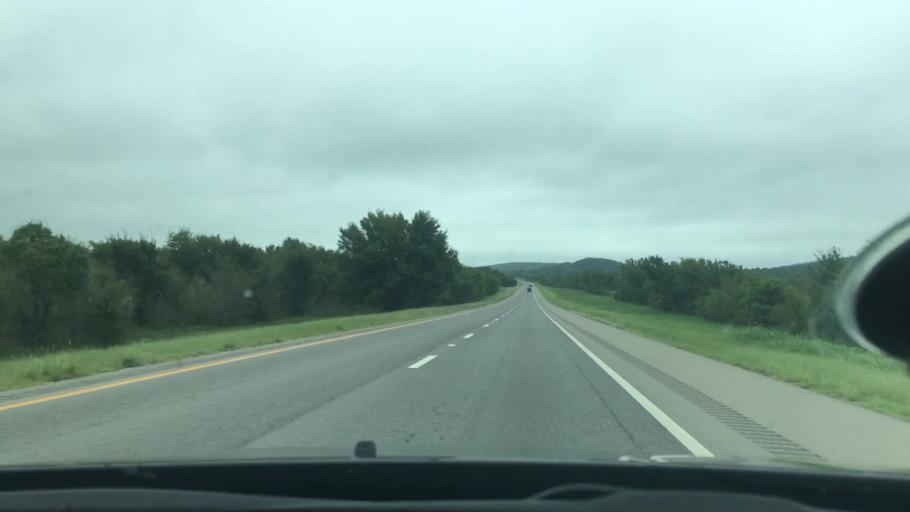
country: US
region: Oklahoma
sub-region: McIntosh County
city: Checotah
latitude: 35.4569
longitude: -95.4184
